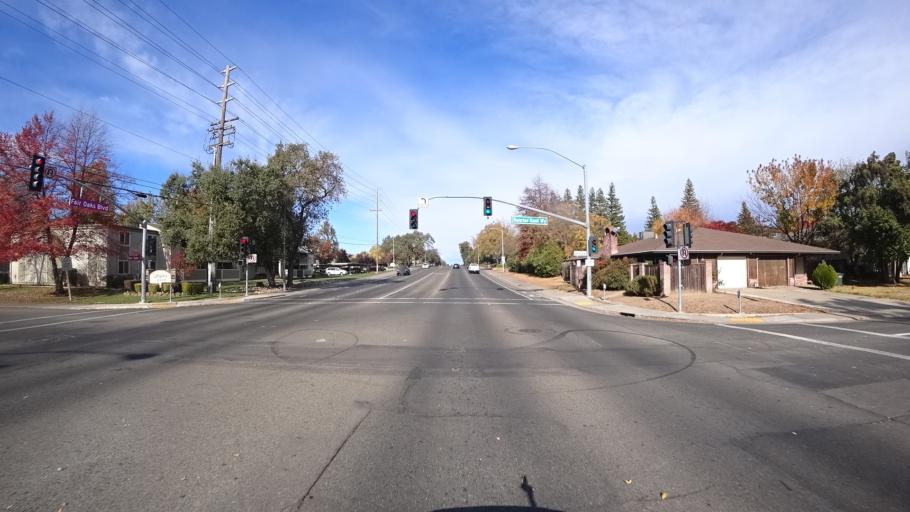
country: US
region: California
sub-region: Sacramento County
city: Fair Oaks
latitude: 38.6721
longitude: -121.2621
